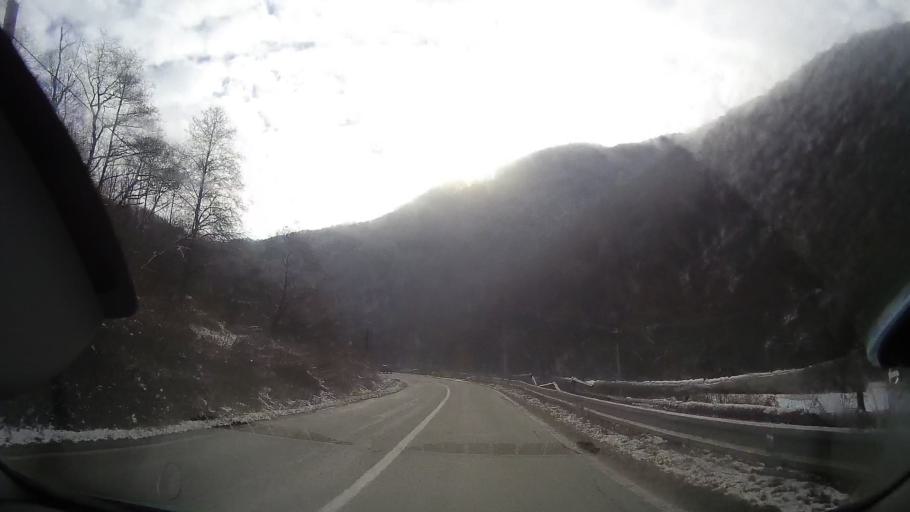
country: RO
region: Alba
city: Salciua de Sus
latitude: 46.4011
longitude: 23.3637
